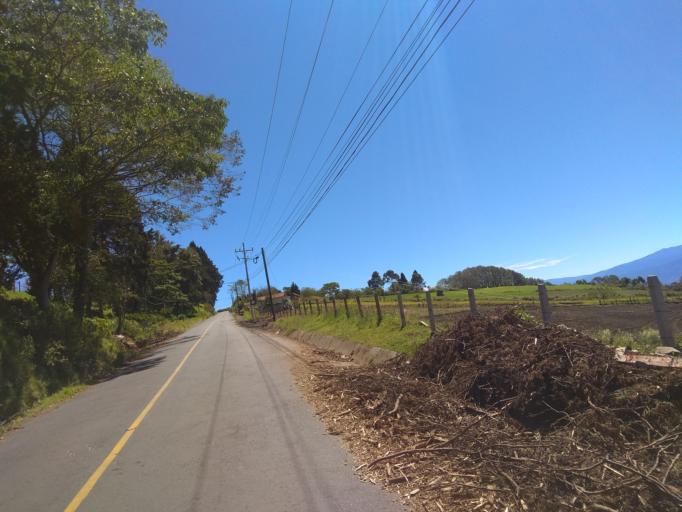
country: CR
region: Cartago
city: Tres Rios
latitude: 9.9421
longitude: -83.9294
